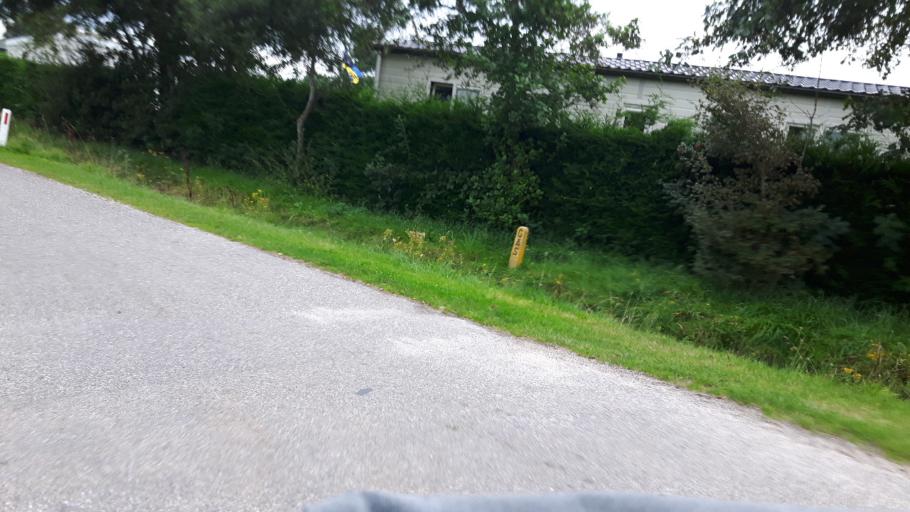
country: NL
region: Friesland
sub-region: Gemeente Ameland
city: Nes
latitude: 53.4535
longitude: 5.8168
